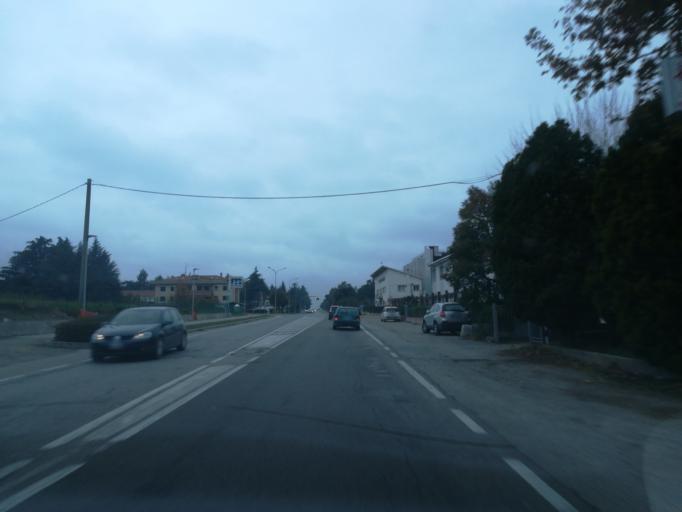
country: IT
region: Emilia-Romagna
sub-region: Provincia di Bologna
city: Toscanella
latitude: 44.3748
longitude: 11.6595
